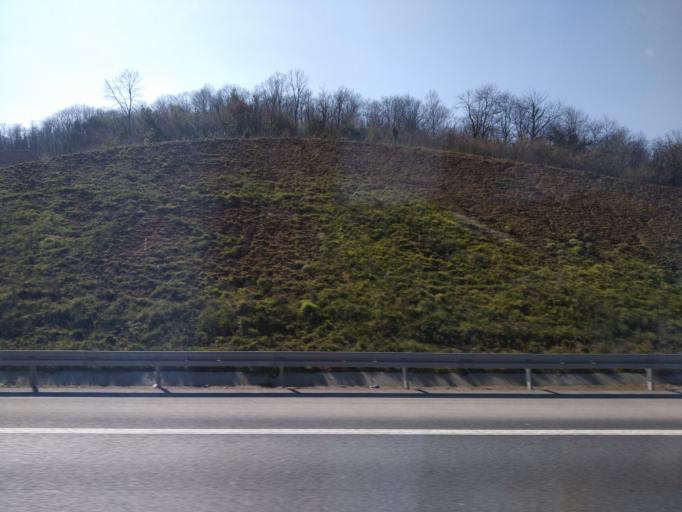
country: TR
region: Istanbul
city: Mahmut Sevket Pasa
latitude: 41.1671
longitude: 29.2532
